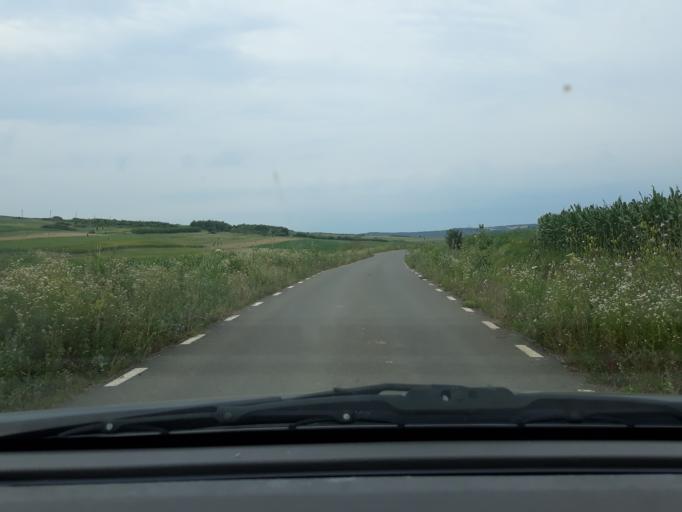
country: RO
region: Salaj
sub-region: Comuna Dobrin
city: Dobrin
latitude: 47.2823
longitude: 23.0918
